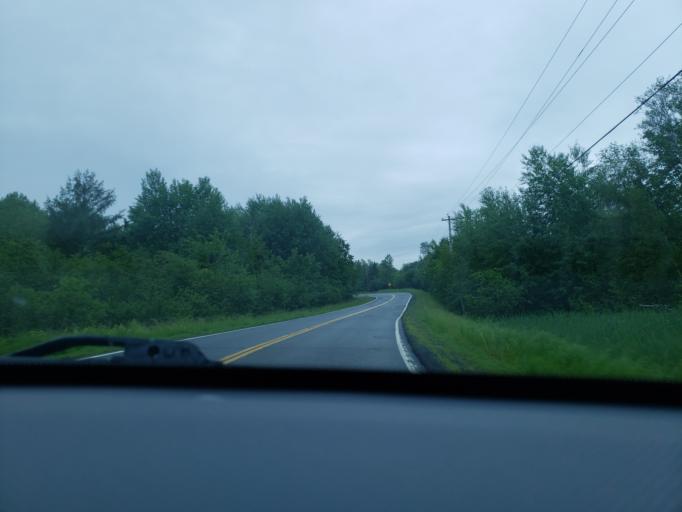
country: CA
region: Nova Scotia
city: Windsor
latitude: 45.0607
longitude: -63.9882
